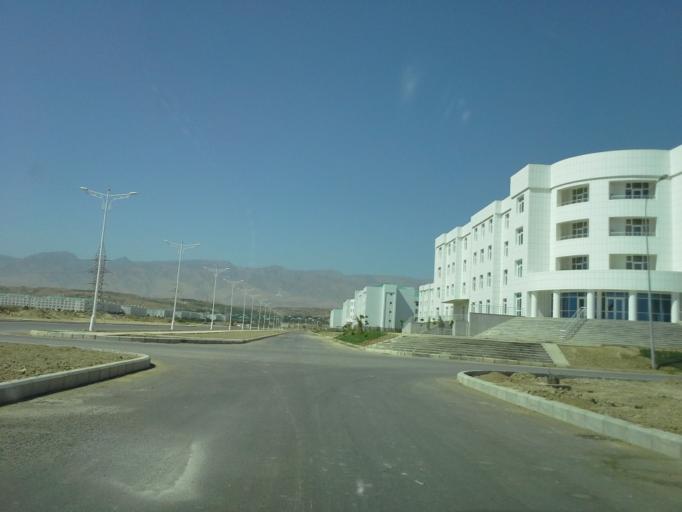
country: TM
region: Ahal
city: Ashgabat
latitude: 37.9754
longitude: 58.3322
